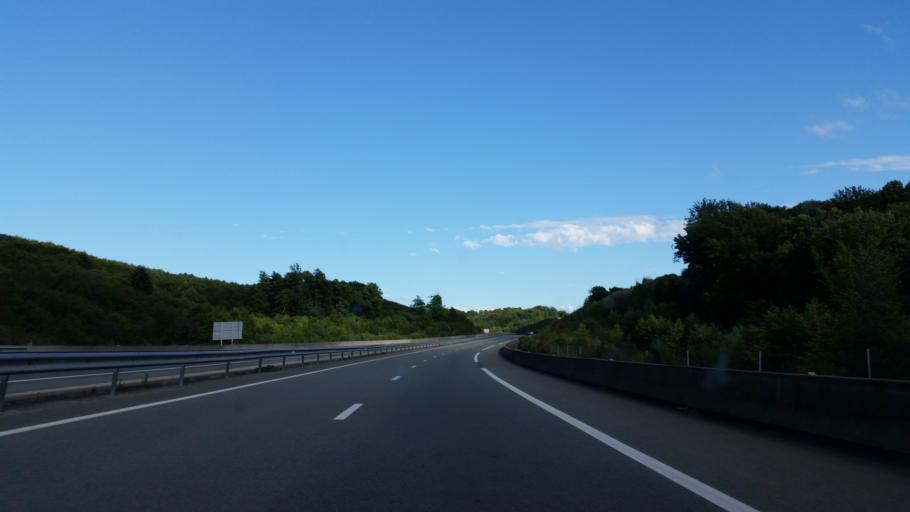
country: FR
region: Franche-Comte
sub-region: Departement de la Haute-Saone
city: Ronchamp
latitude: 47.6217
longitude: 6.6605
